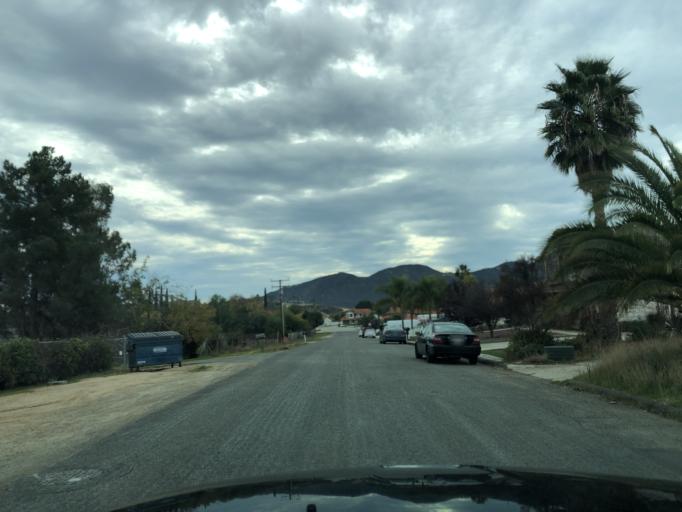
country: US
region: California
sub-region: Riverside County
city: Wildomar
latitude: 33.6178
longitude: -117.2798
